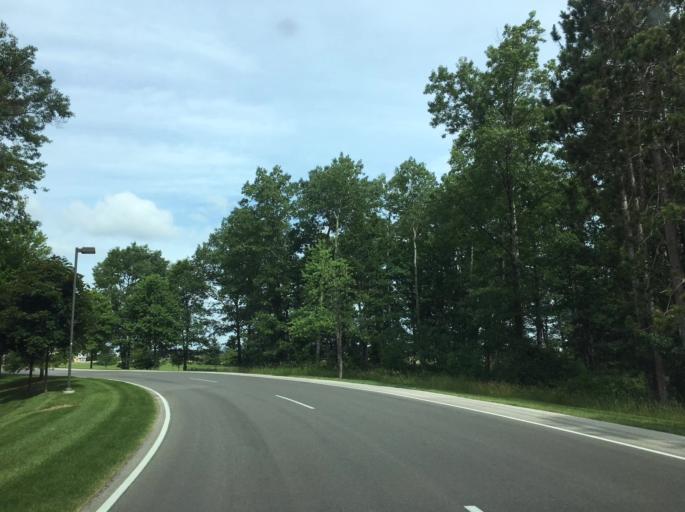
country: US
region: Michigan
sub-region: Grand Traverse County
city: Traverse City
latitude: 44.7361
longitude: -85.5746
